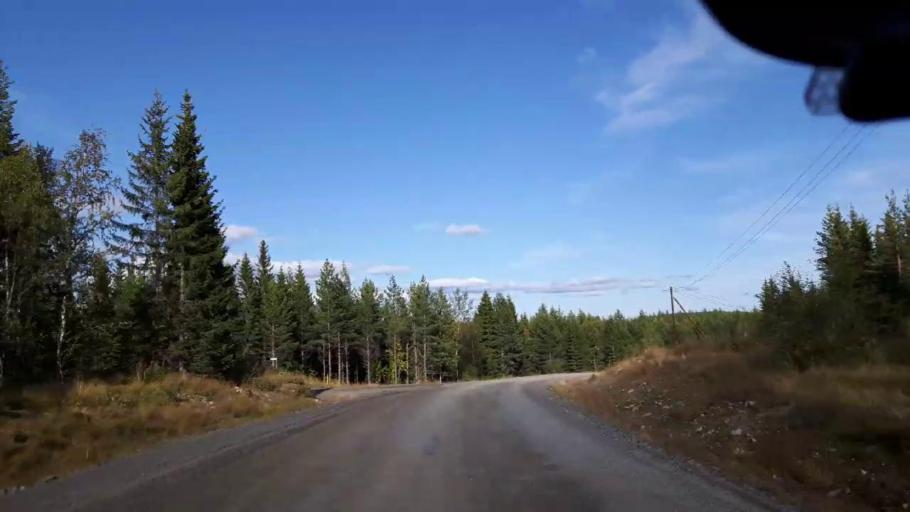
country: SE
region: Jaemtland
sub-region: Ragunda Kommun
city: Hammarstrand
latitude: 63.4275
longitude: 16.1655
